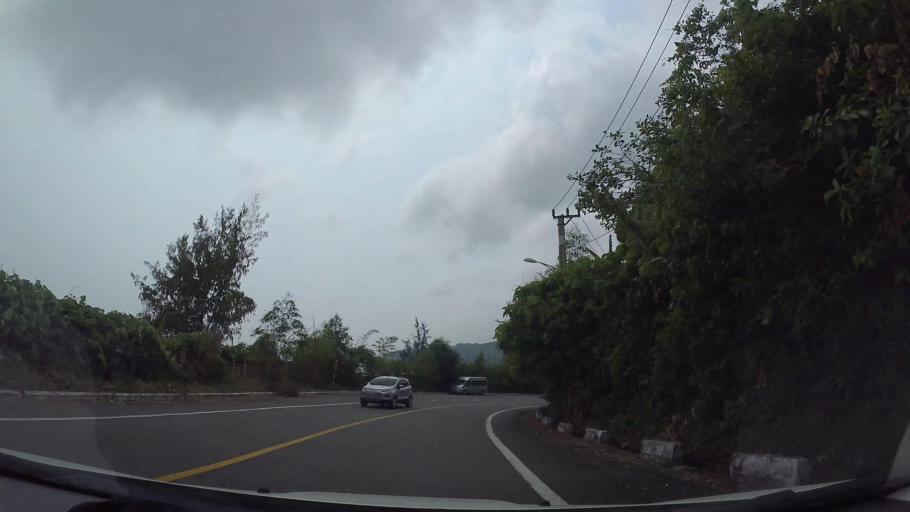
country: VN
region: Da Nang
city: Son Tra
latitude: 16.1062
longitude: 108.2964
